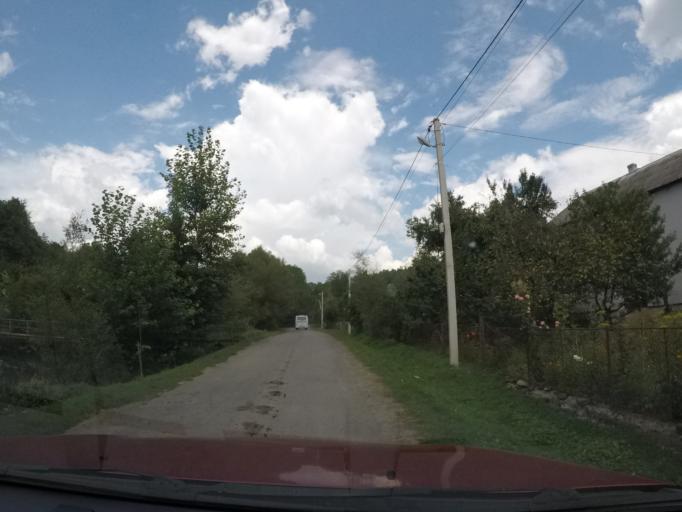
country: UA
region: Zakarpattia
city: Velykyi Bereznyi
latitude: 49.0183
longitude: 22.6185
